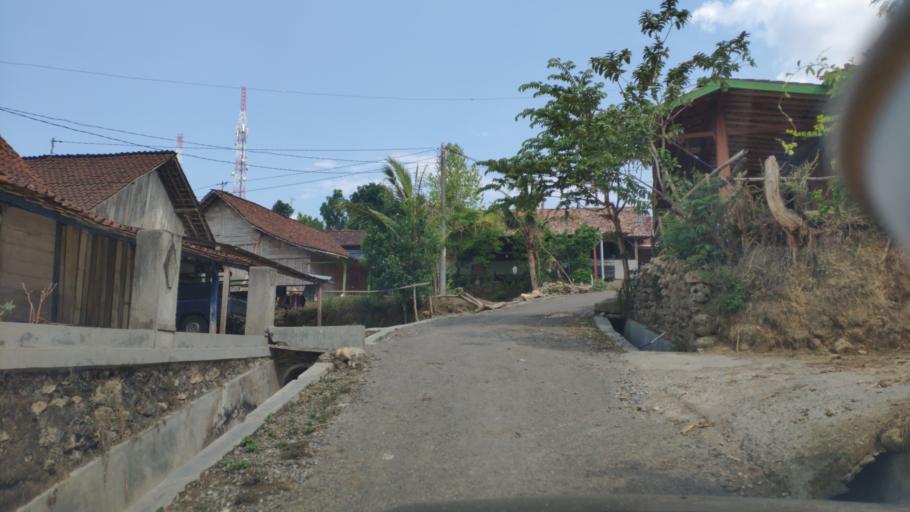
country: ID
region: Central Java
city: Semanggi
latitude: -7.0580
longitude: 111.4264
